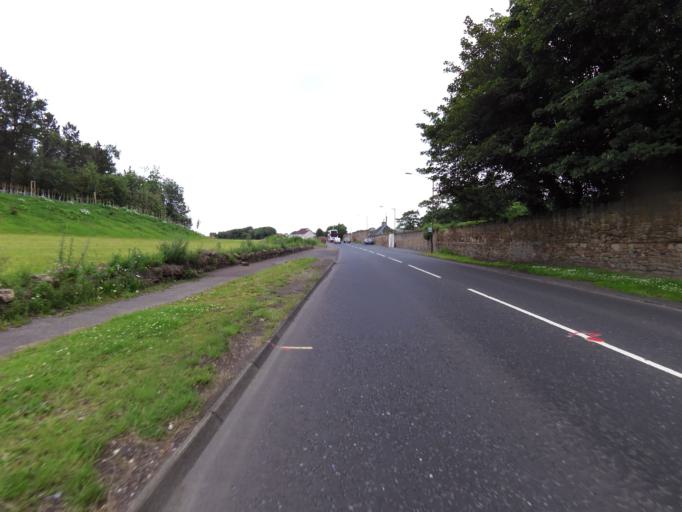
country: GB
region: Scotland
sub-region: East Lothian
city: Prestonpans
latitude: 55.9540
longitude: -3.0005
